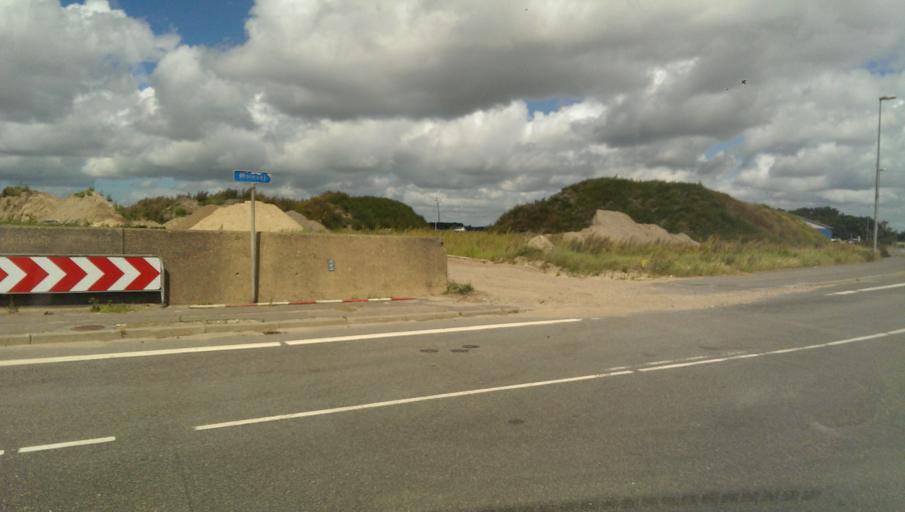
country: DK
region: South Denmark
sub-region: Esbjerg Kommune
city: Esbjerg
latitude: 55.4818
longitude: 8.4191
